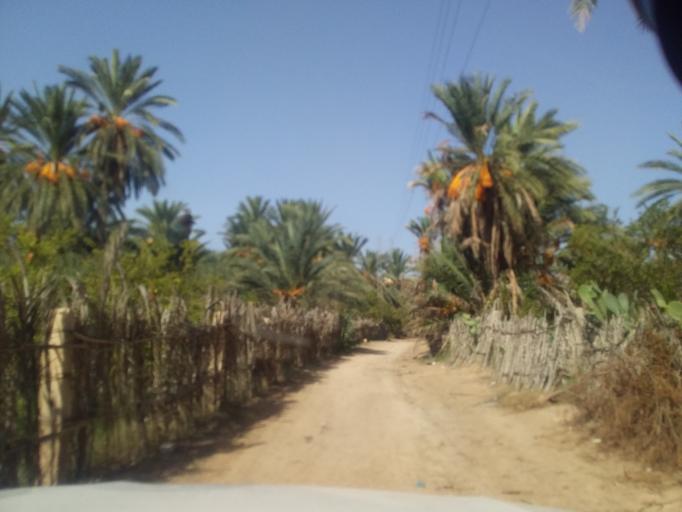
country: TN
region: Qabis
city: Gabes
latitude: 33.6253
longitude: 10.2848
